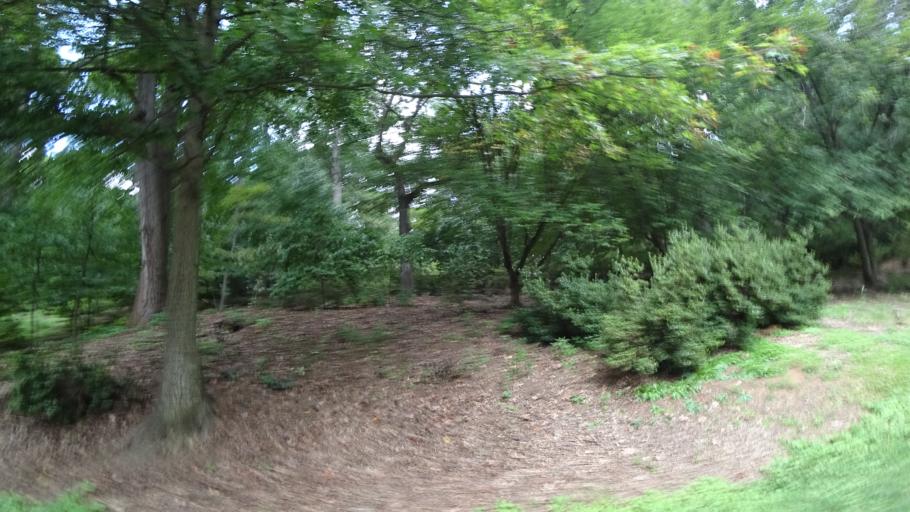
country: US
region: Maryland
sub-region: Prince George's County
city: Mount Rainier
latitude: 38.9087
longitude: -76.9738
